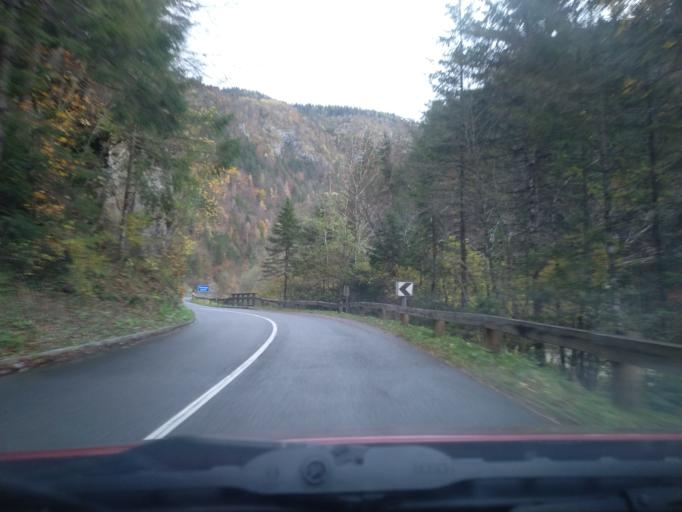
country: SI
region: Luce
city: Luce
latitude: 46.3654
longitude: 14.7326
